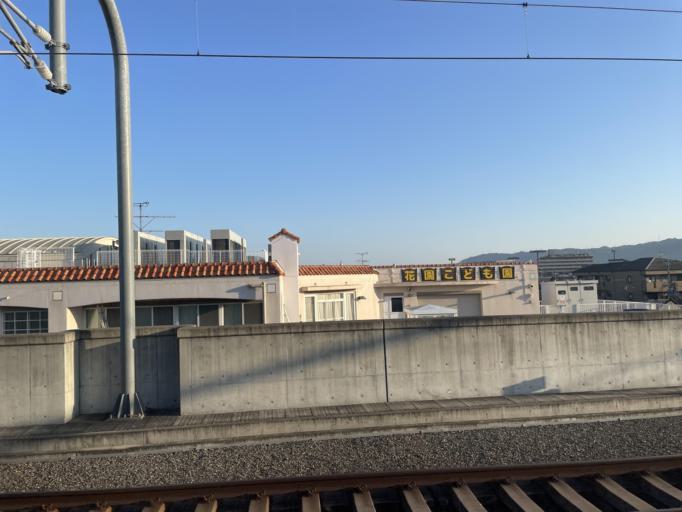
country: JP
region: Osaka
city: Daitocho
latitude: 34.6626
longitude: 135.6228
